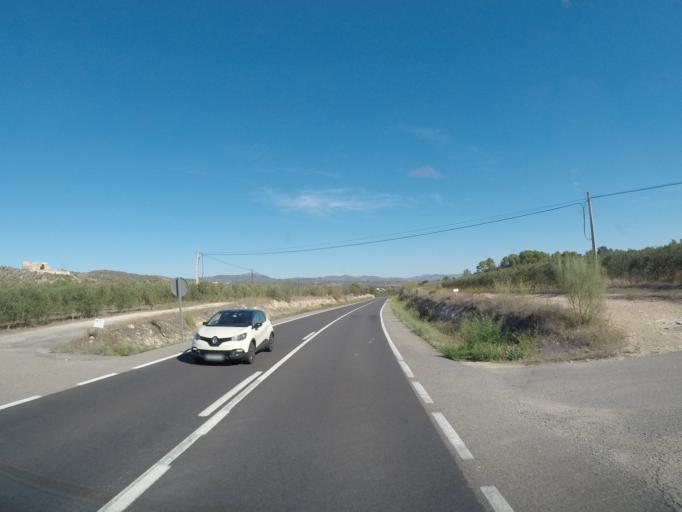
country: ES
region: Catalonia
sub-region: Provincia de Tarragona
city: Miravet
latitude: 41.0274
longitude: 0.6039
